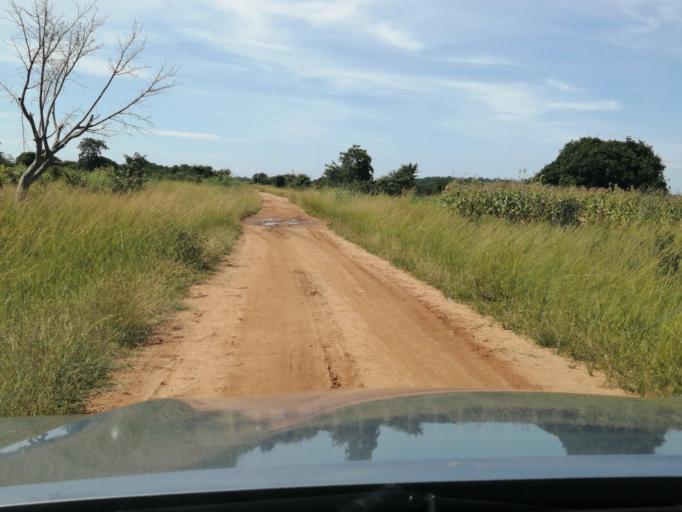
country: ZM
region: Central
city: Chibombo
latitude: -14.9848
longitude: 27.8095
